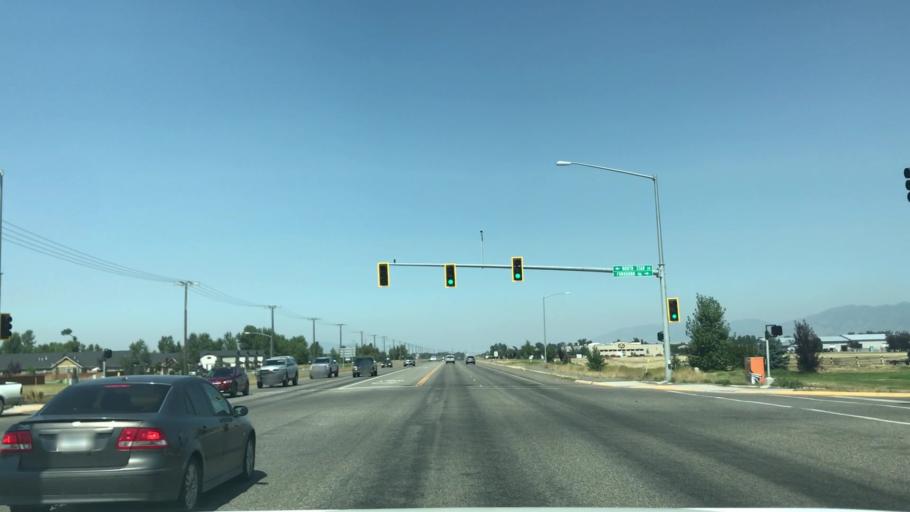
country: US
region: Montana
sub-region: Gallatin County
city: Four Corners
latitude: 45.6787
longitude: -111.1857
